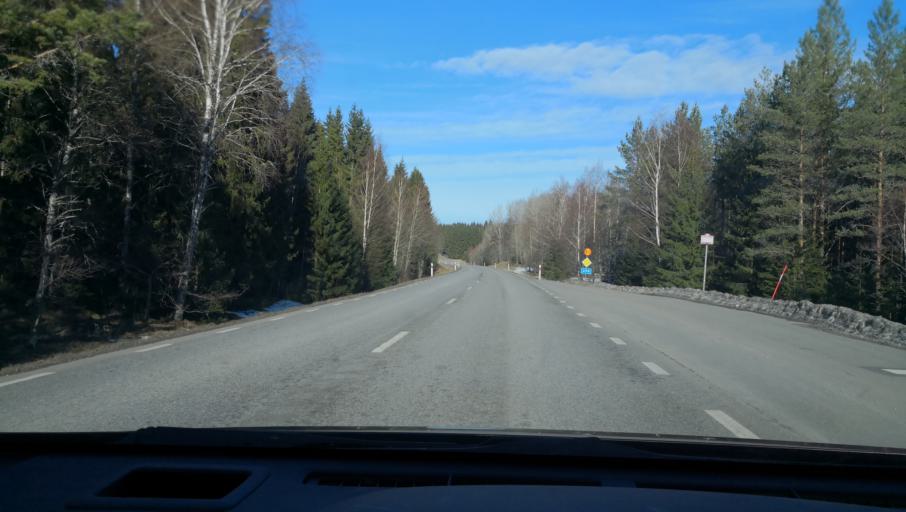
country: SE
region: Uppsala
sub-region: Uppsala Kommun
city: Vattholma
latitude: 60.0251
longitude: 17.7484
